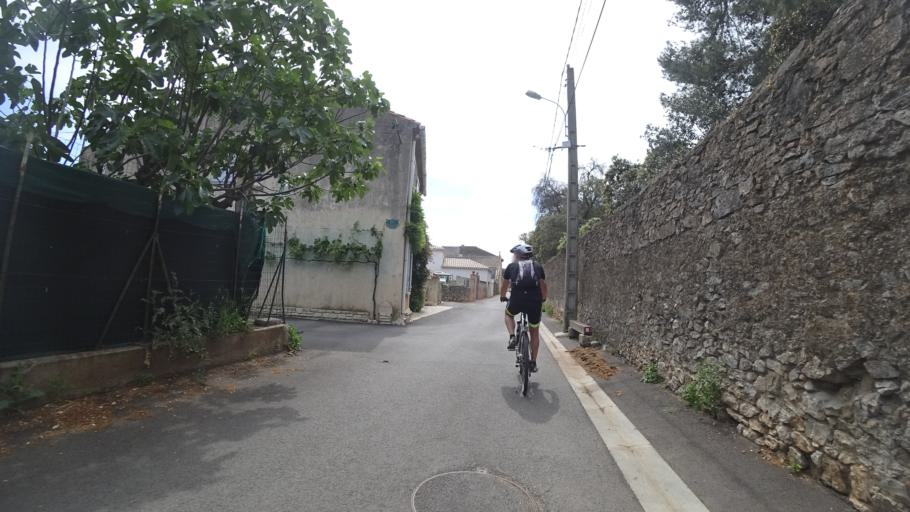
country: FR
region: Languedoc-Roussillon
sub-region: Departement de l'Aude
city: Canet
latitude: 43.2513
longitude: 2.8283
